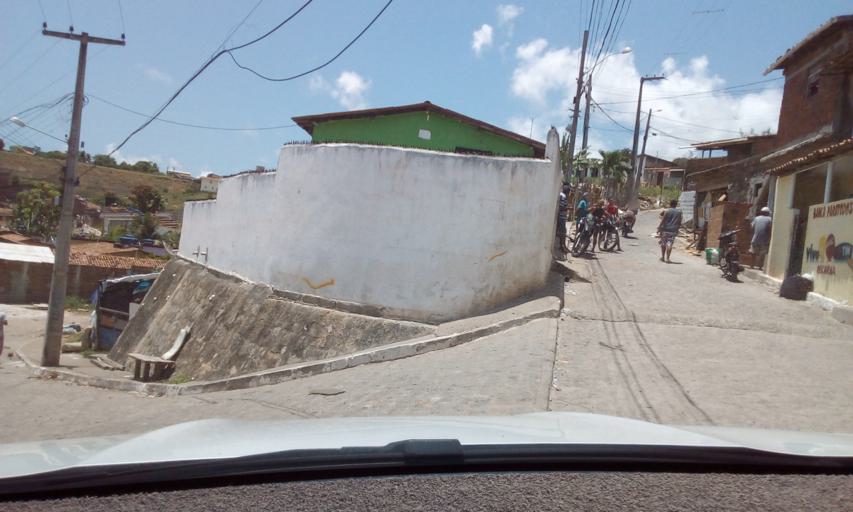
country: BR
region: Paraiba
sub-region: Joao Pessoa
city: Joao Pessoa
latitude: -7.1462
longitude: -34.8293
